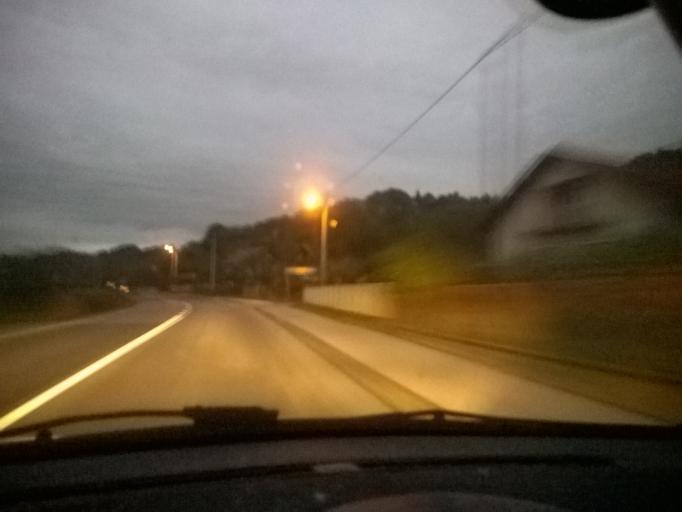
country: HR
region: Krapinsko-Zagorska
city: Zabok
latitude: 46.0343
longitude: 15.9289
